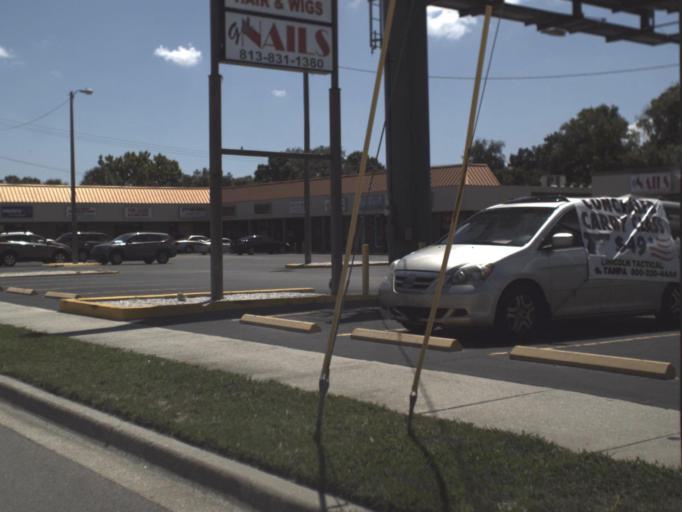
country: US
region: Florida
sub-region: Hillsborough County
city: Tampa
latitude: 27.8829
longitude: -82.5066
